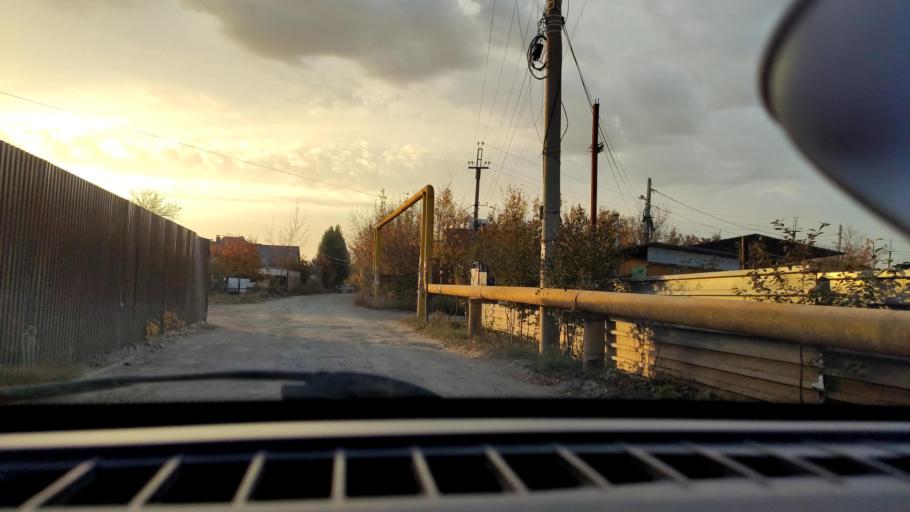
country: RU
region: Samara
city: Samara
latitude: 53.2729
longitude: 50.2284
